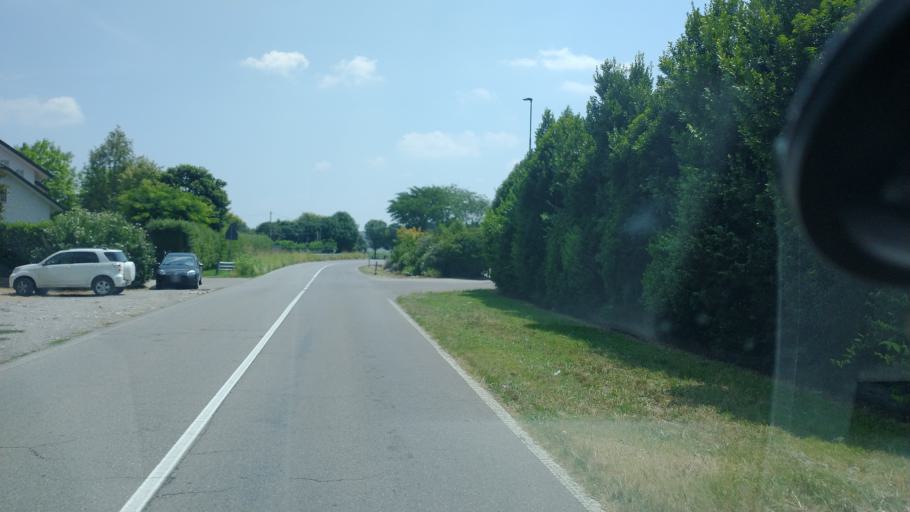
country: IT
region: Lombardy
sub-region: Provincia di Bergamo
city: Calvenzano
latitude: 45.4898
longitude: 9.5991
